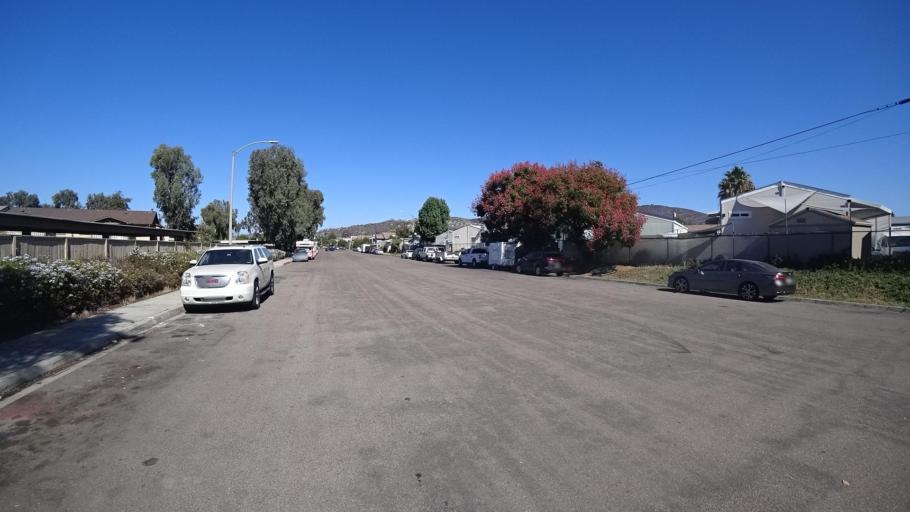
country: US
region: California
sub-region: San Diego County
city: El Cajon
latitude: 32.8154
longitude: -116.9588
